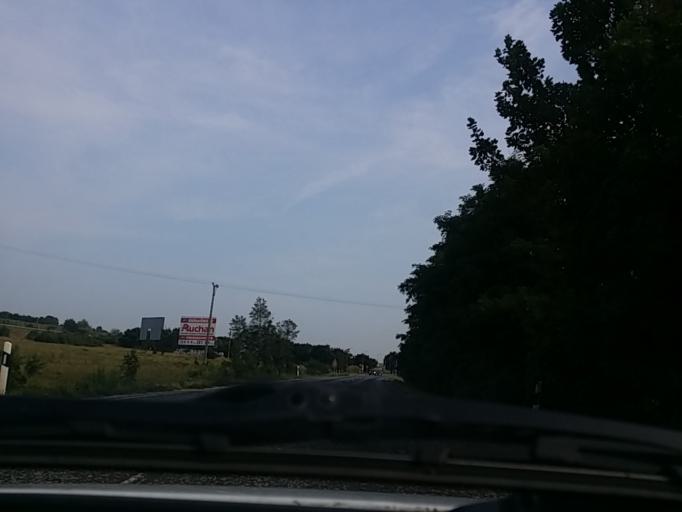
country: HU
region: Pest
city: Biatorbagy
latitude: 47.4846
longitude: 18.8347
